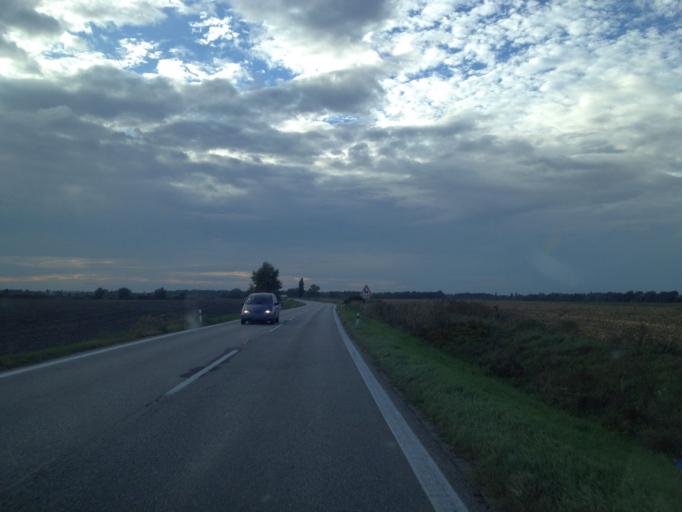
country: SK
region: Nitriansky
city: Komarno
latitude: 47.7620
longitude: 18.1835
